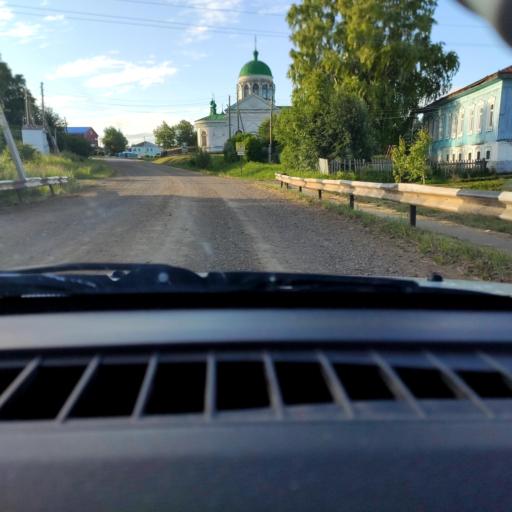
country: RU
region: Perm
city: Uinskoye
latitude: 57.1186
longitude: 56.5221
